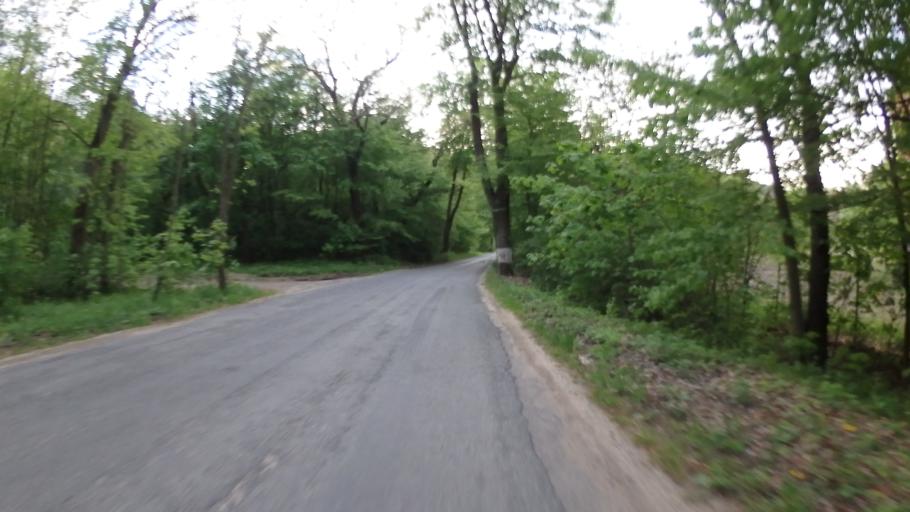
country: CZ
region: South Moravian
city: Strelice
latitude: 49.1382
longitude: 16.4678
